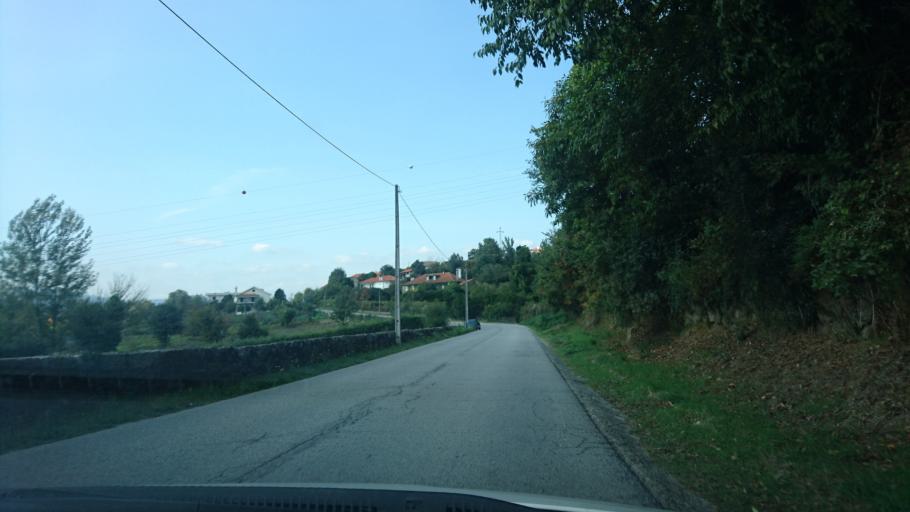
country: PT
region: Vila Real
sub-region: Mondim de Basto
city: Mondim de Basto
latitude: 41.4556
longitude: -7.9236
